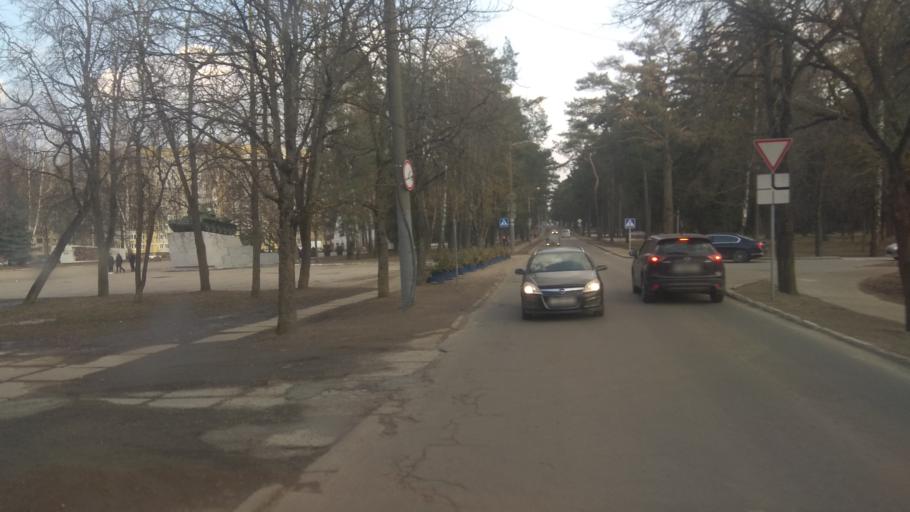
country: BY
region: Minsk
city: Lyeskawka
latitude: 53.9467
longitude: 27.7120
